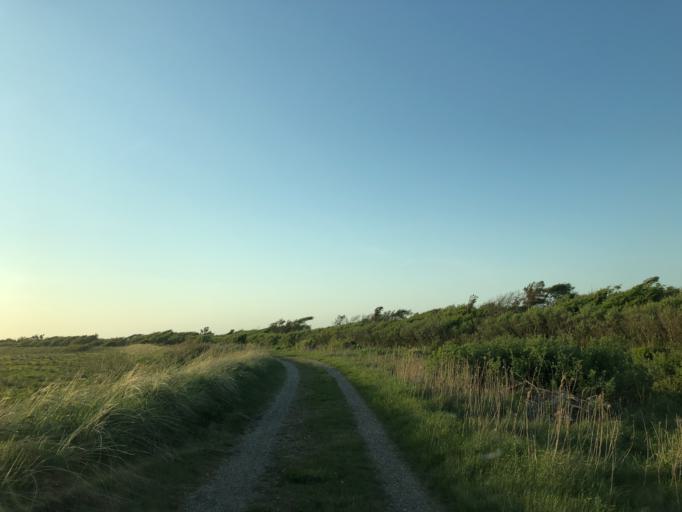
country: DK
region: Central Jutland
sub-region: Holstebro Kommune
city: Ulfborg
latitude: 56.2384
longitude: 8.1687
